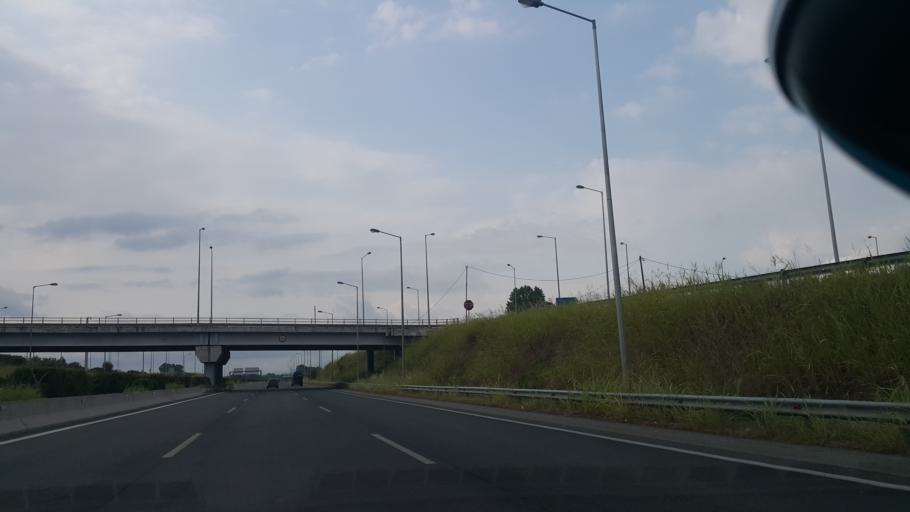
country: GR
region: Central Macedonia
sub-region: Nomos Pierias
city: Nea Efesos
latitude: 40.1947
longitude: 22.5487
